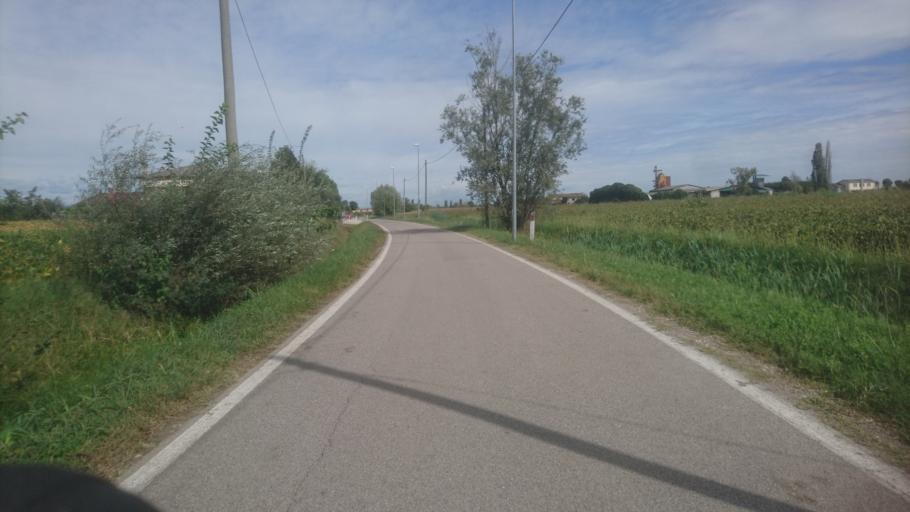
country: IT
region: Veneto
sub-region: Provincia di Padova
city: Selvazzano Dentro
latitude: 45.4028
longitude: 11.7763
